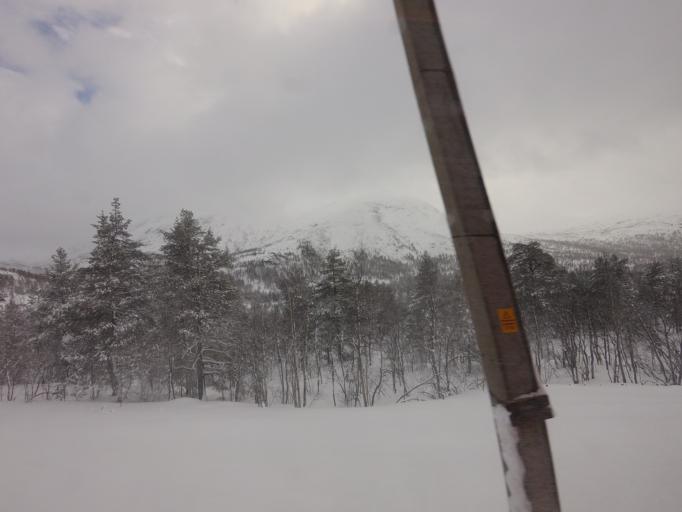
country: NO
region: Hordaland
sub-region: Ulvik
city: Ulvik
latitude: 60.7027
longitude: 6.8834
